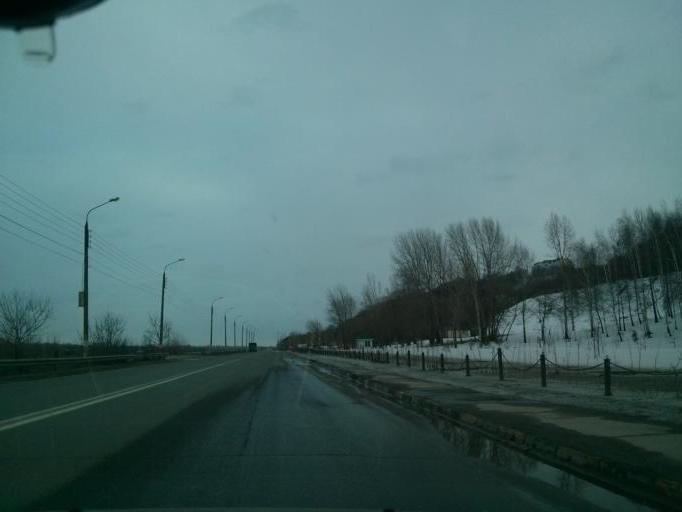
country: RU
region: Nizjnij Novgorod
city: Bor
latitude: 56.3247
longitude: 44.0517
